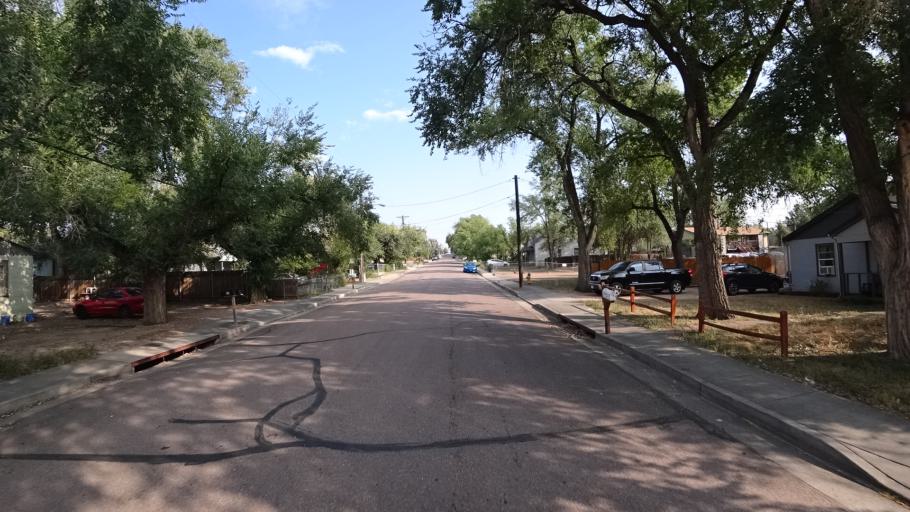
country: US
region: Colorado
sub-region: El Paso County
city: Colorado Springs
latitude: 38.8446
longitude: -104.7804
